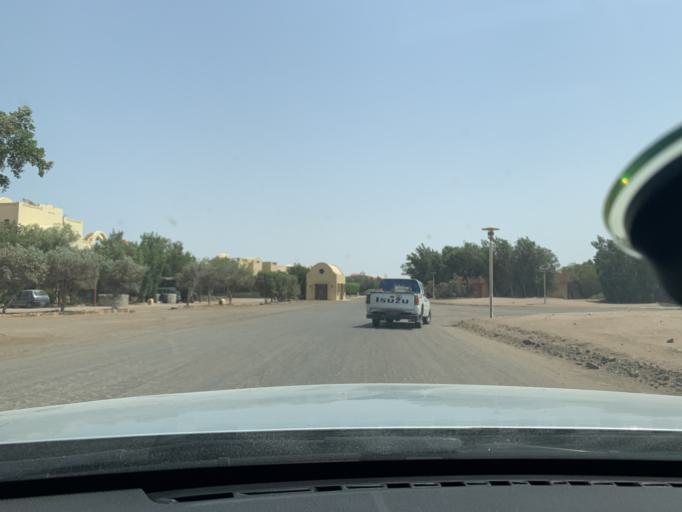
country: EG
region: Red Sea
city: El Gouna
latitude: 27.3879
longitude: 33.6692
